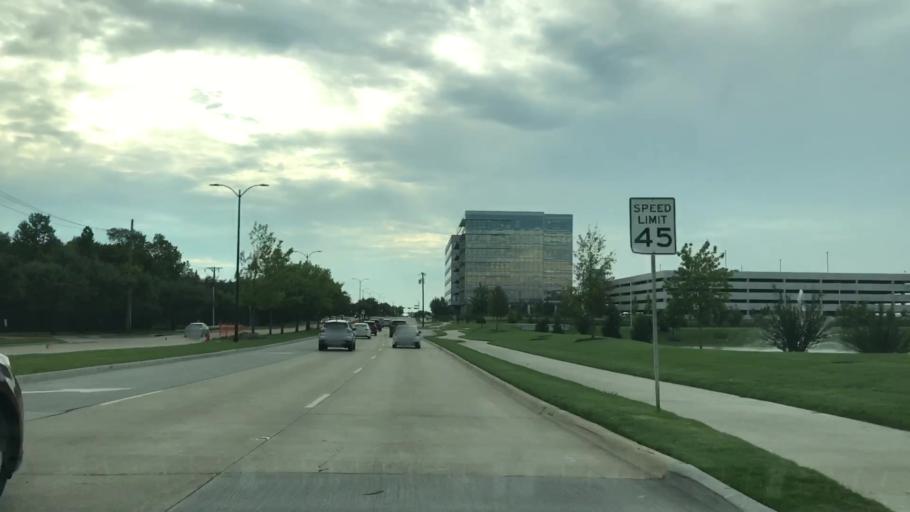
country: US
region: Texas
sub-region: Collin County
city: Frisco
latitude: 33.1068
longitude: -96.8296
